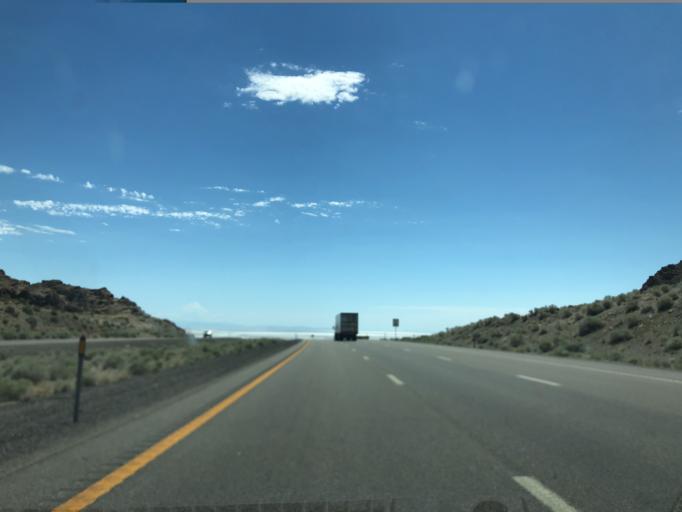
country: US
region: Nevada
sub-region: Elko County
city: West Wendover
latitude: 40.7464
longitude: -114.1050
